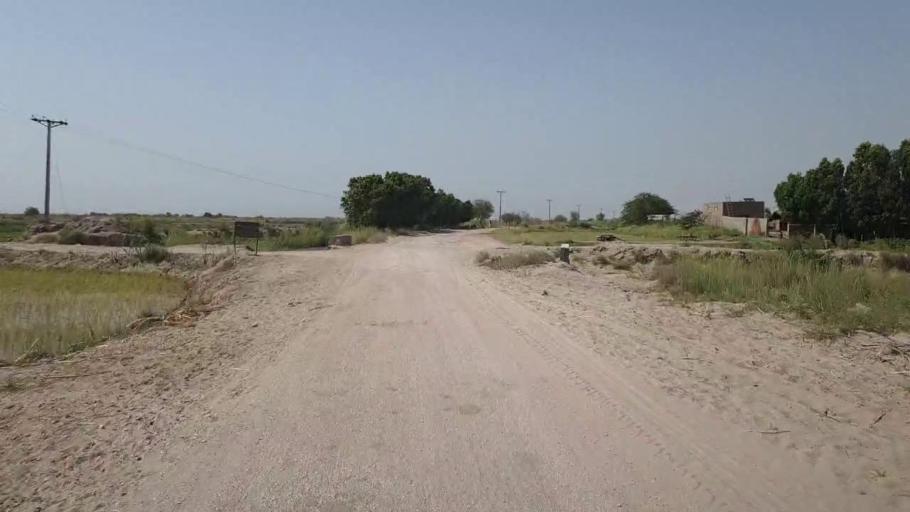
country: PK
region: Sindh
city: Jam Sahib
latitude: 26.4204
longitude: 68.9073
